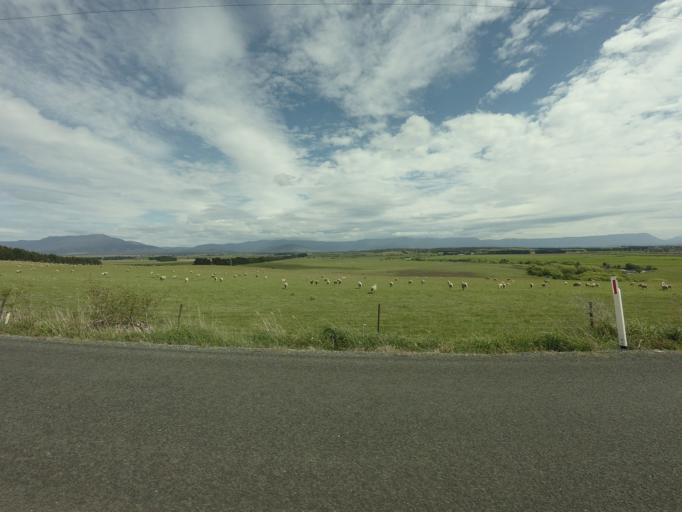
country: AU
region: Tasmania
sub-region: Northern Midlands
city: Longford
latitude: -41.7659
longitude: 147.2121
